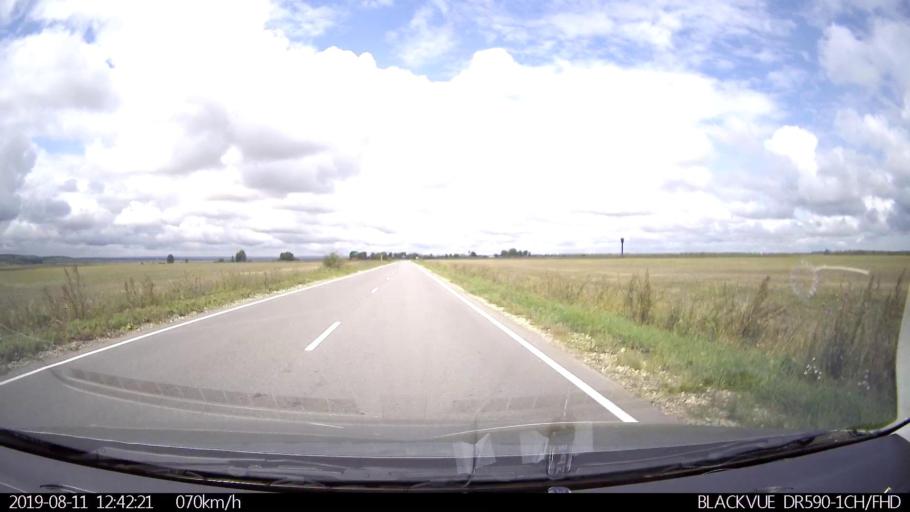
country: RU
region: Ulyanovsk
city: Ignatovka
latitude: 53.8452
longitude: 47.7525
